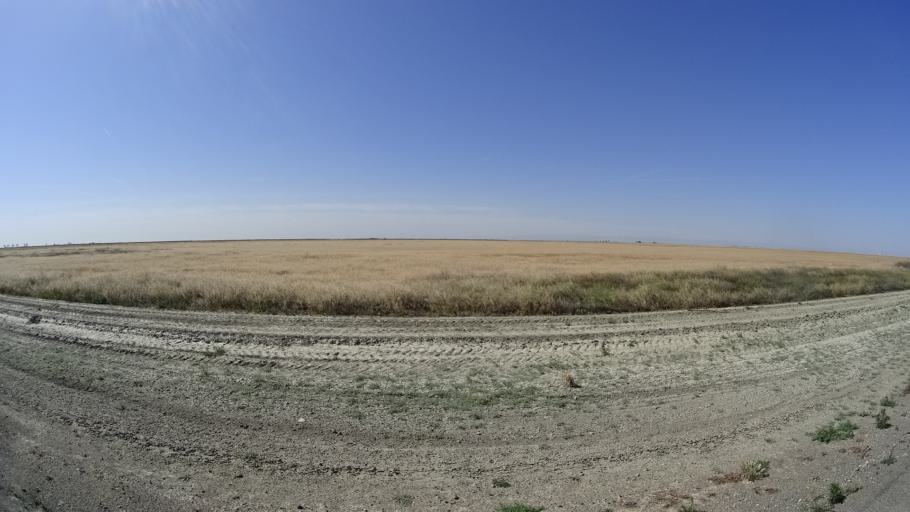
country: US
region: California
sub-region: Tulare County
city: Alpaugh
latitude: 35.8914
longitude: -119.5406
